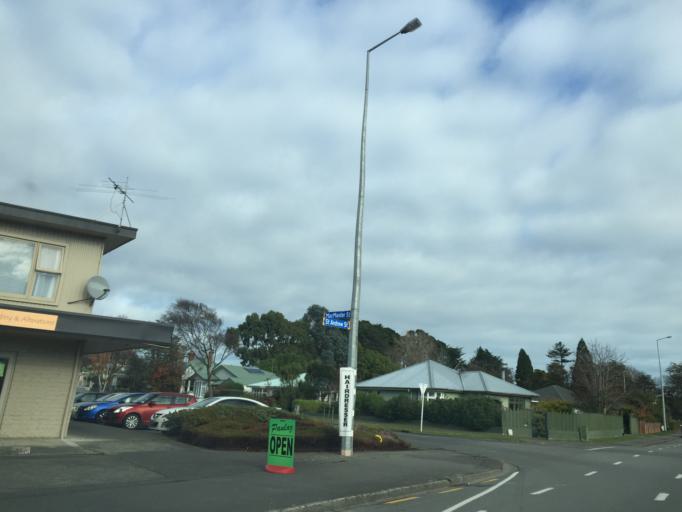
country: NZ
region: Southland
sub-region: Invercargill City
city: Invercargill
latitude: -46.4035
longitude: 168.3632
